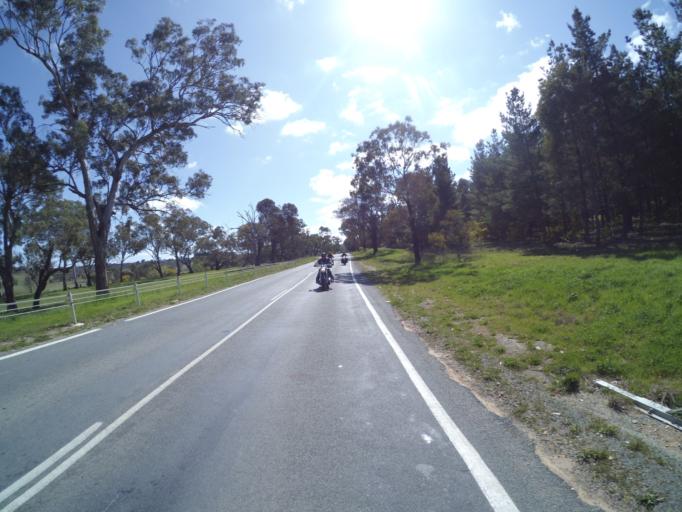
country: AU
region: New South Wales
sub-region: Queanbeyan
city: Queanbeyan
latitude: -35.3010
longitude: 149.2523
